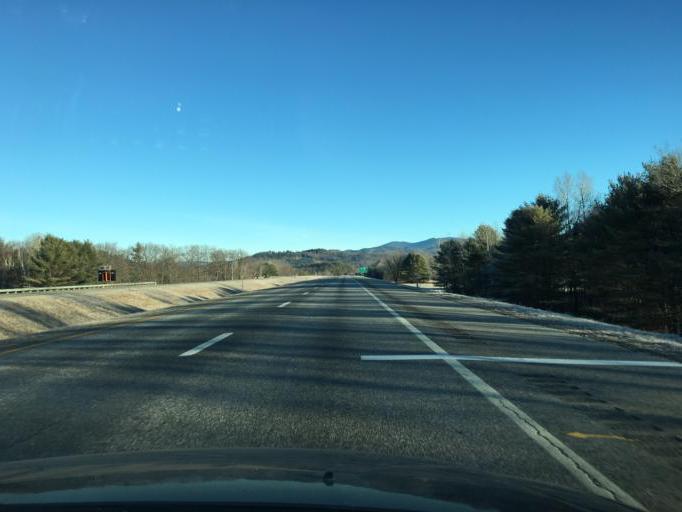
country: US
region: New Hampshire
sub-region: Grafton County
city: Thornton
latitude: 43.8300
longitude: -71.6555
